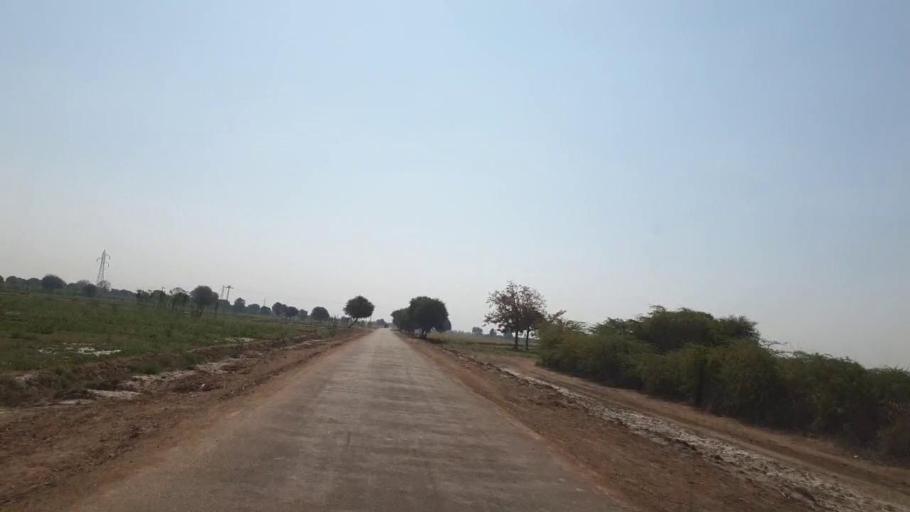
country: PK
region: Sindh
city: Kunri
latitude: 25.1657
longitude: 69.5467
